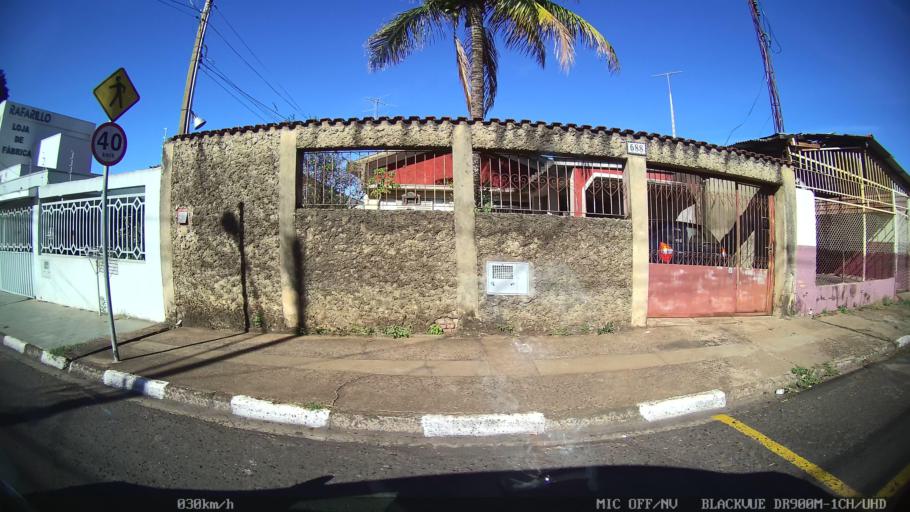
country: BR
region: Sao Paulo
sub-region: Franca
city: Franca
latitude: -20.5299
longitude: -47.4069
